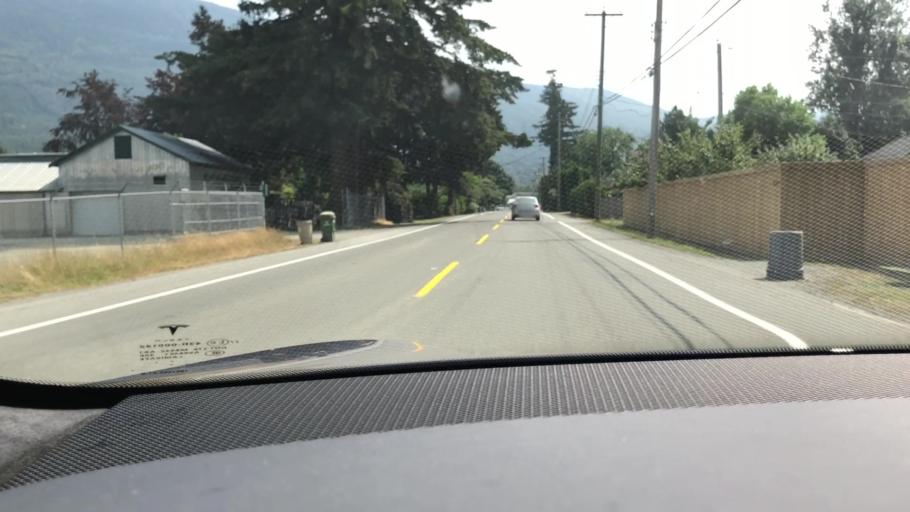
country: CA
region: British Columbia
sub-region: Fraser Valley Regional District
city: Chilliwack
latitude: 49.0858
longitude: -122.0649
